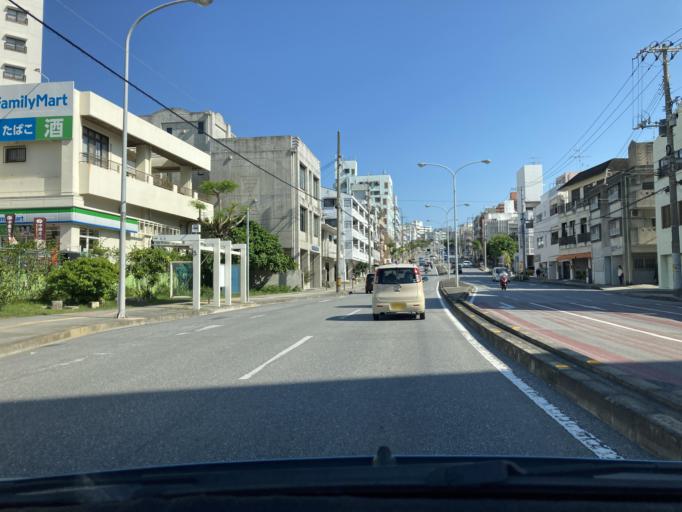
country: JP
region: Okinawa
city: Naha-shi
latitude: 26.2062
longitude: 127.7007
